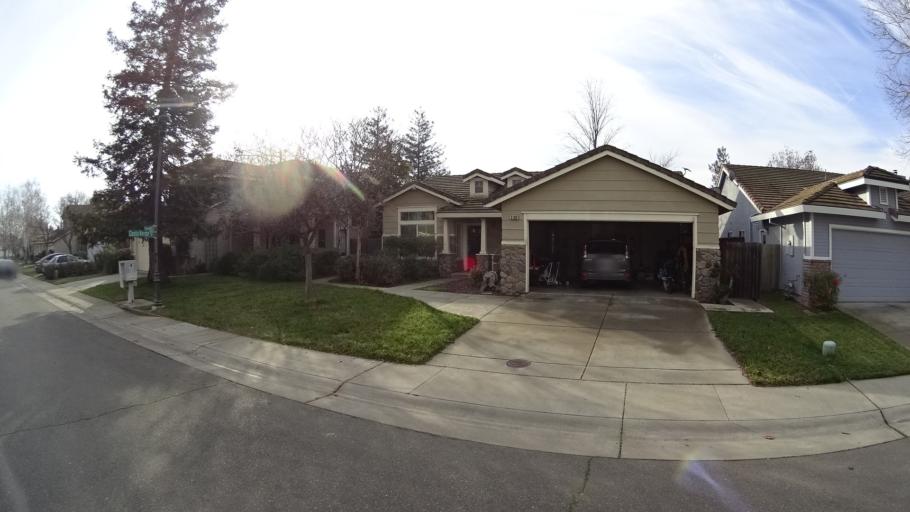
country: US
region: California
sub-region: Yolo County
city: Davis
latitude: 38.5598
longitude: -121.7119
